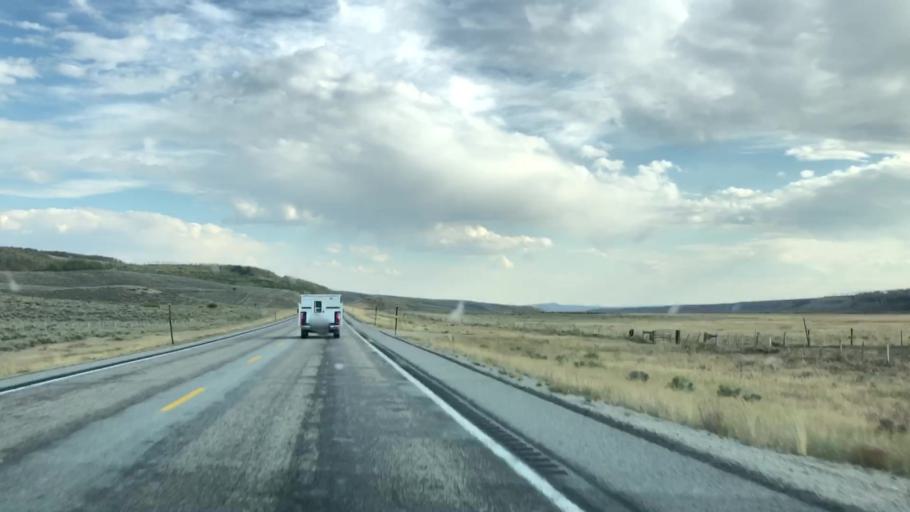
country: US
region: Wyoming
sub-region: Sublette County
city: Pinedale
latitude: 43.0983
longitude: -110.1682
